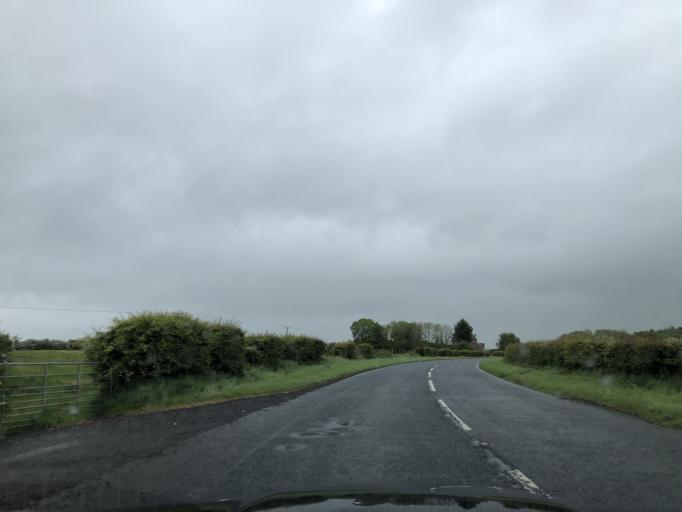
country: GB
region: Northern Ireland
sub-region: Moyle District
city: Ballycastle
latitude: 55.1806
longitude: -6.3245
